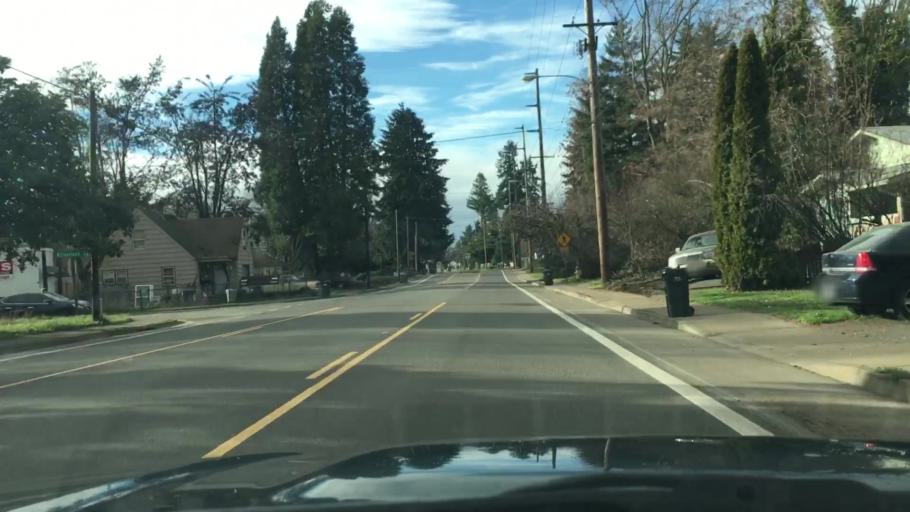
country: US
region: Oregon
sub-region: Lane County
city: Eugene
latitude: 44.0636
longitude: -123.1268
